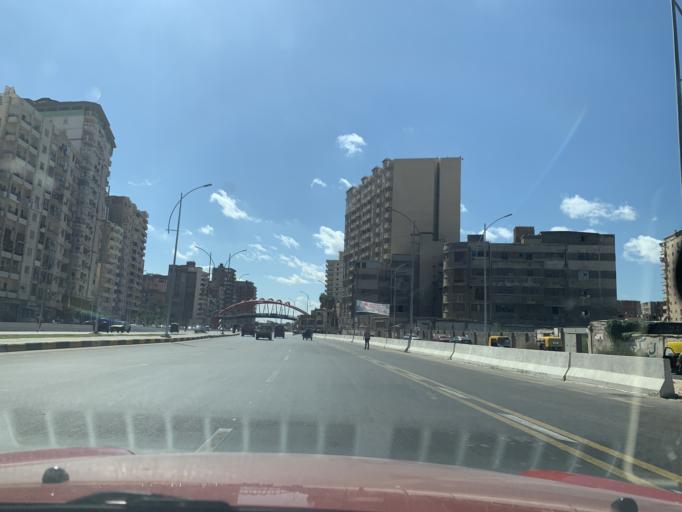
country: EG
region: Alexandria
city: Alexandria
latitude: 31.1960
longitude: 29.9338
